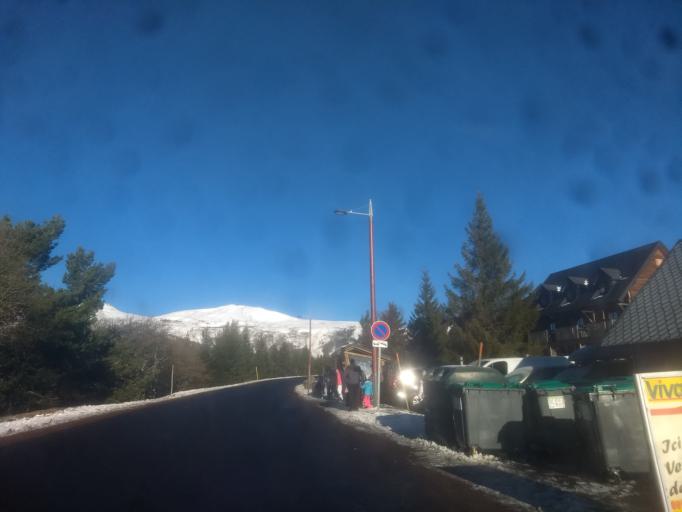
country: FR
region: Auvergne
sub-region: Departement du Puy-de-Dome
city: Mont-Dore
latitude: 45.5038
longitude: 2.8631
